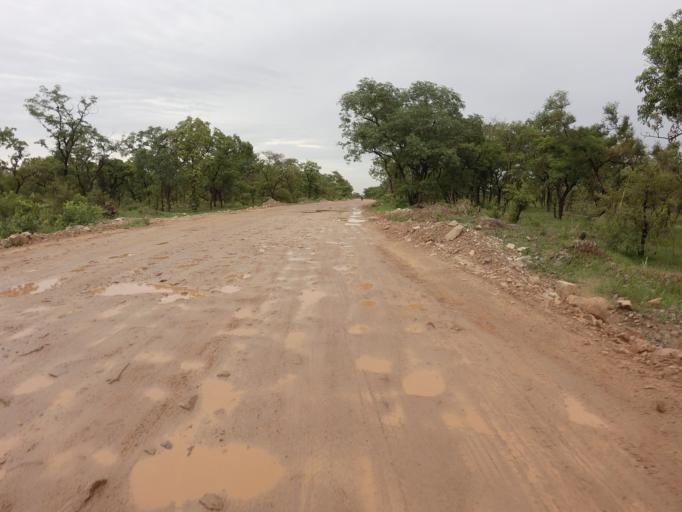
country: GH
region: Upper East
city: Bolgatanga
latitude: 10.8783
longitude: -0.6355
